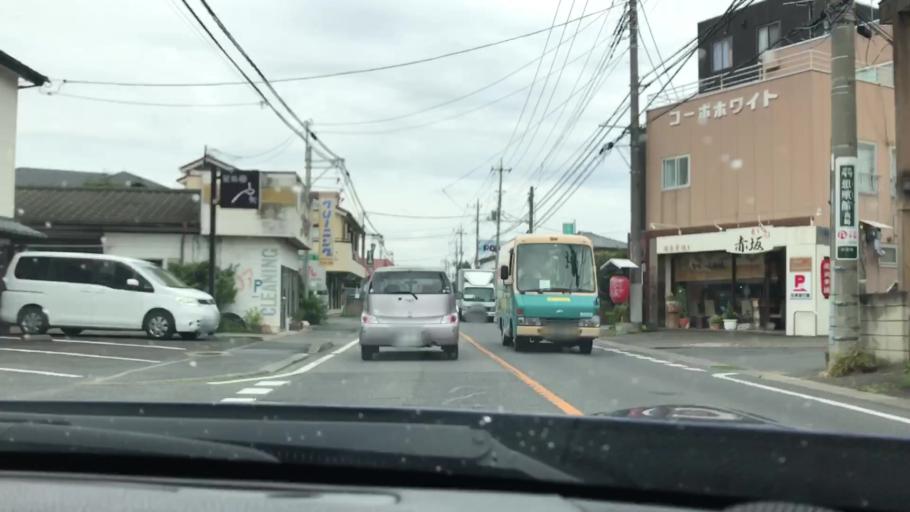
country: JP
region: Gunma
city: Takasaki
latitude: 36.3488
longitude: 139.0224
